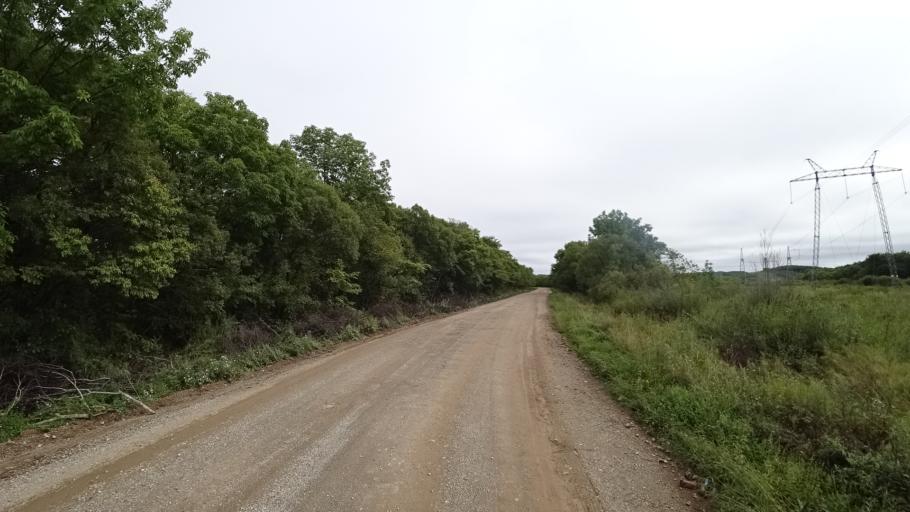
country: RU
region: Primorskiy
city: Lyalichi
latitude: 44.0786
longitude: 132.4535
